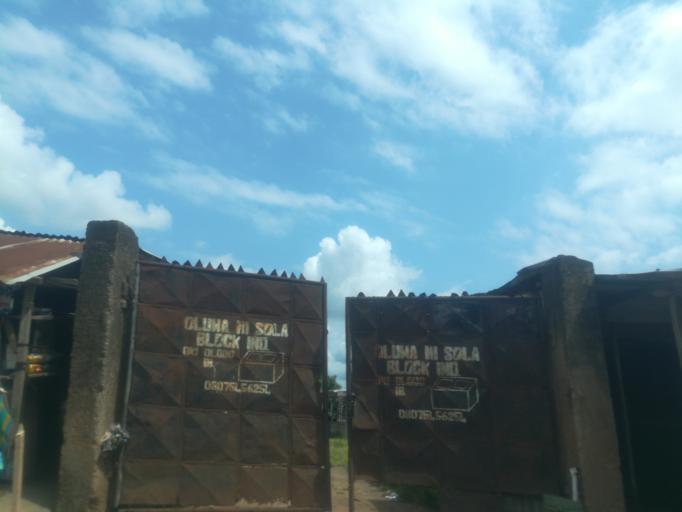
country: NG
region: Oyo
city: Egbeda
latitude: 7.4238
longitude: 3.9963
